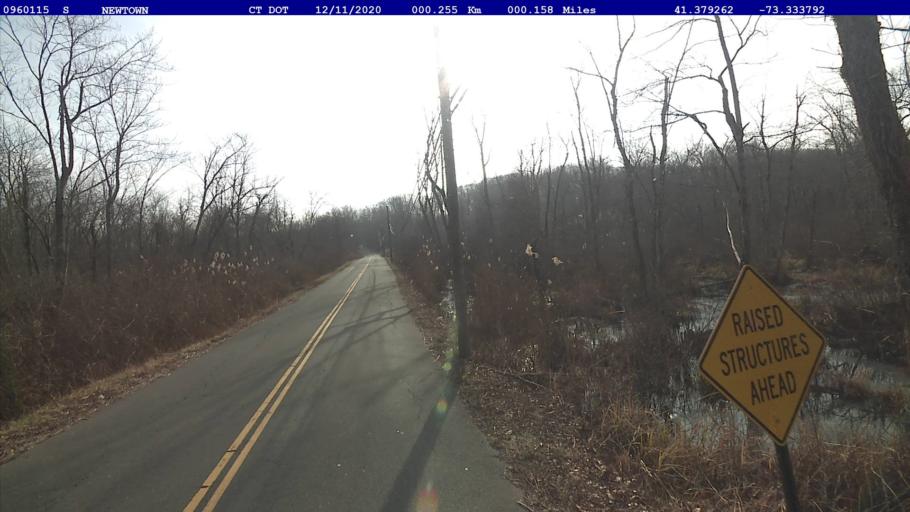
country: US
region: Connecticut
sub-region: Fairfield County
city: Newtown
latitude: 41.3793
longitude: -73.3338
